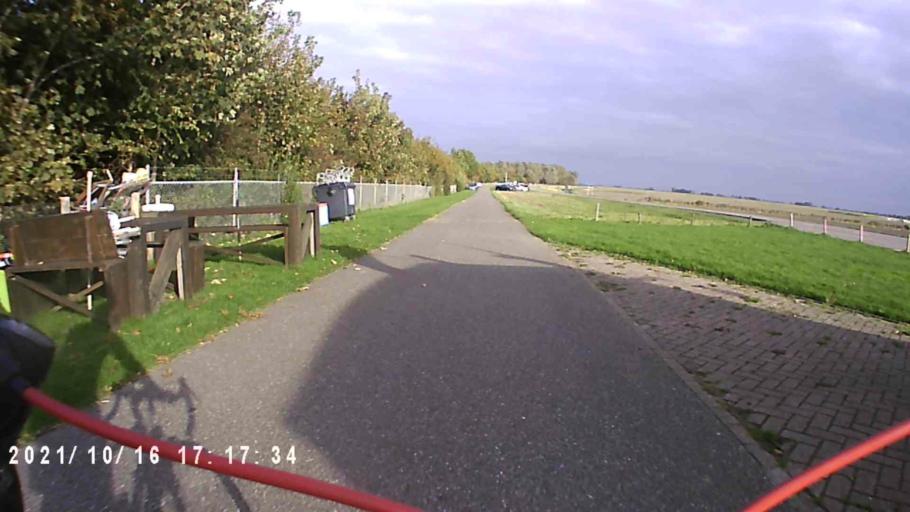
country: NL
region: Friesland
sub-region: Gemeente Kollumerland en Nieuwkruisland
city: Kollum
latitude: 53.3165
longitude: 6.1624
